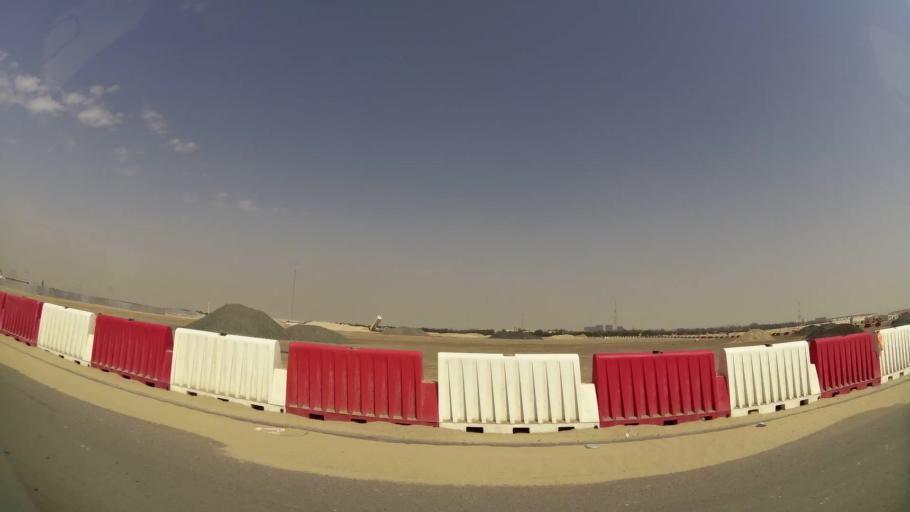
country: AE
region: Abu Dhabi
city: Abu Dhabi
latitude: 24.3152
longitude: 54.5835
